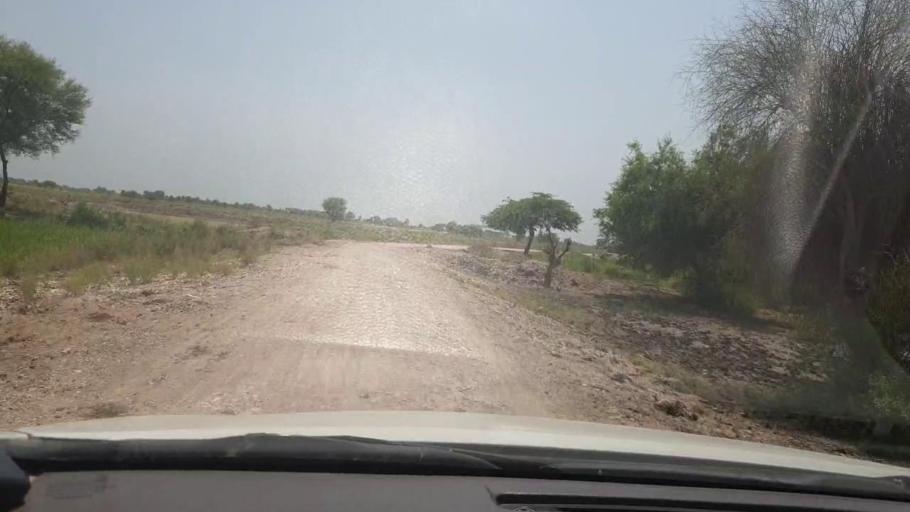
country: PK
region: Sindh
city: Garhi Yasin
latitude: 27.9190
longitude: 68.5543
